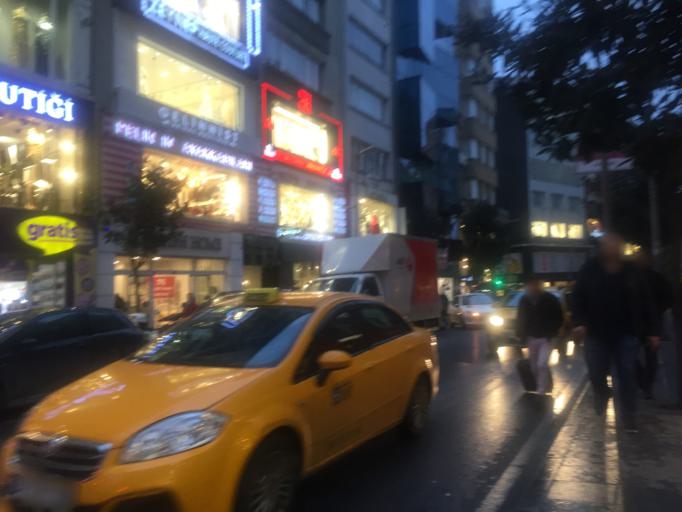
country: TR
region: Istanbul
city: Sisli
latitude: 41.0530
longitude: 28.9897
